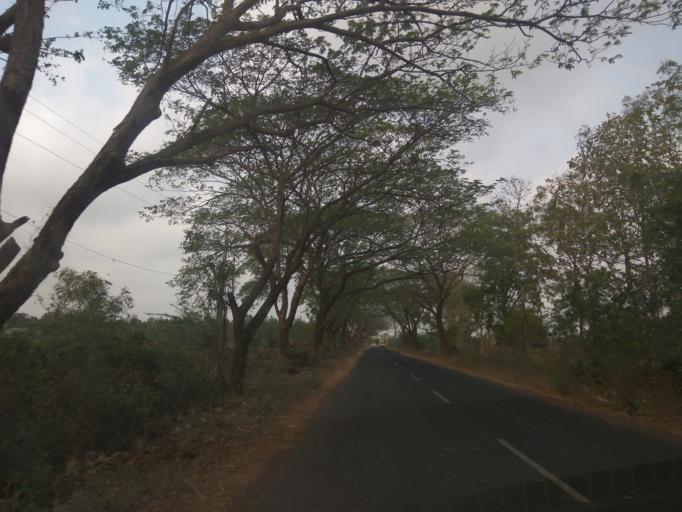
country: IN
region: Andhra Pradesh
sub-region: Prakasam
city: Kandukur
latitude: 15.2060
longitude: 79.8624
